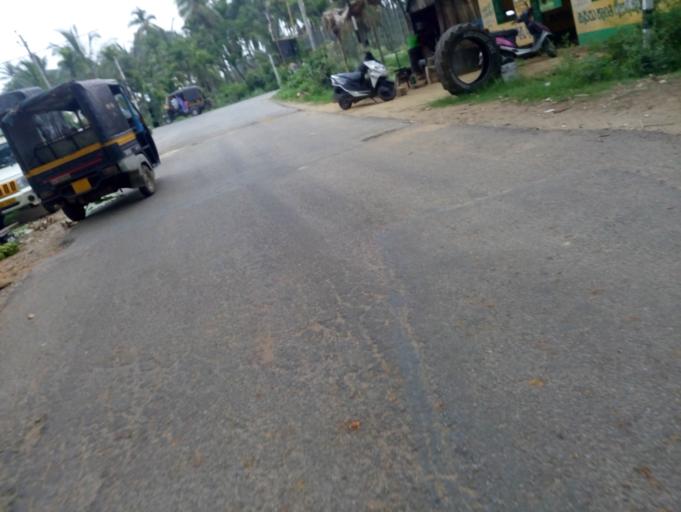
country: IN
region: Karnataka
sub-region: Tumkur
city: Turuvekere
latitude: 13.1762
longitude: 76.6703
